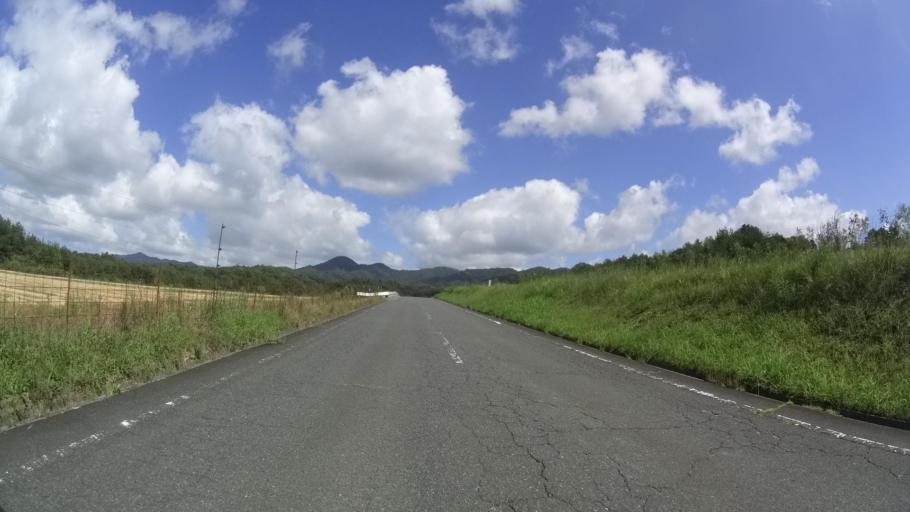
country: JP
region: Kyoto
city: Miyazu
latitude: 35.6724
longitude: 135.1046
